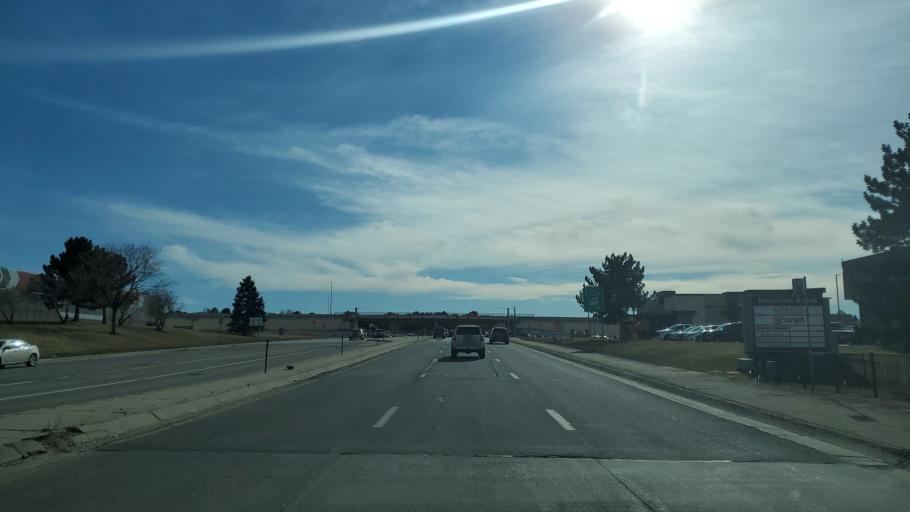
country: US
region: Colorado
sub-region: Douglas County
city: Highlands Ranch
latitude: 39.5657
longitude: -104.9606
